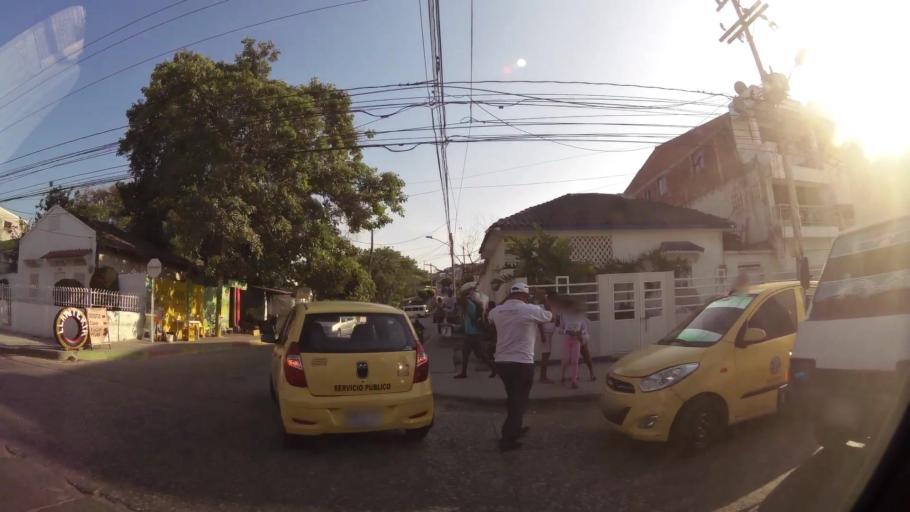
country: CO
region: Bolivar
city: Cartagena
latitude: 10.4377
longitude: -75.5251
